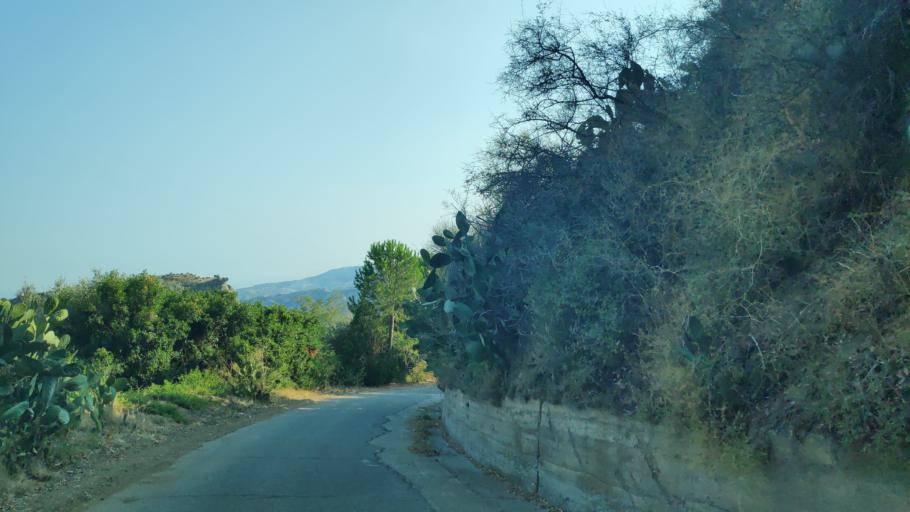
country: IT
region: Calabria
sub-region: Provincia di Reggio Calabria
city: Placanica
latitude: 38.4100
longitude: 16.4297
